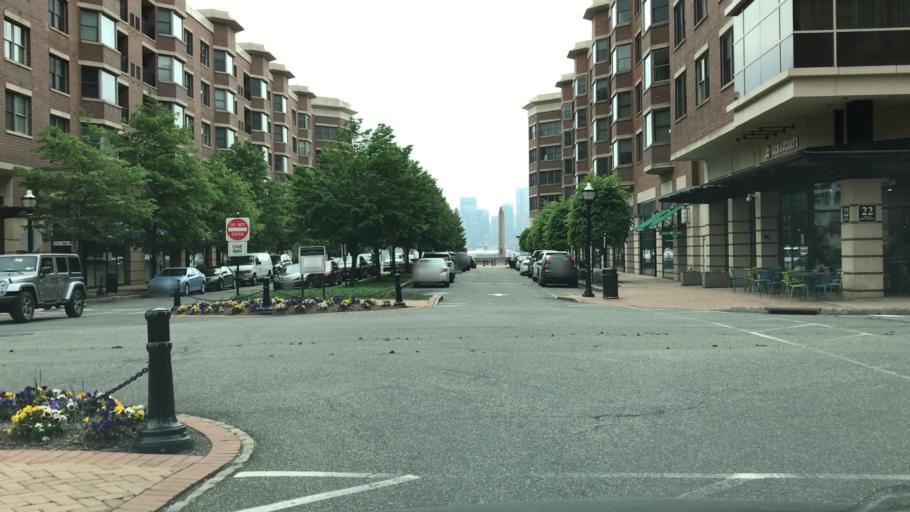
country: US
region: New Jersey
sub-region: Hudson County
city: West New York
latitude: 40.7819
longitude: -74.0062
